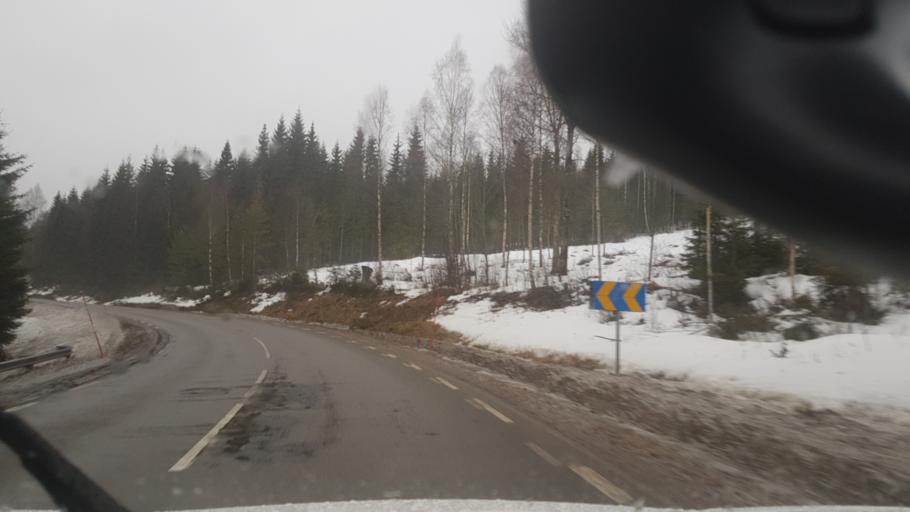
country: SE
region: Vaermland
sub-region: Arjangs Kommun
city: Arjaeng
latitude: 59.5622
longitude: 12.1750
